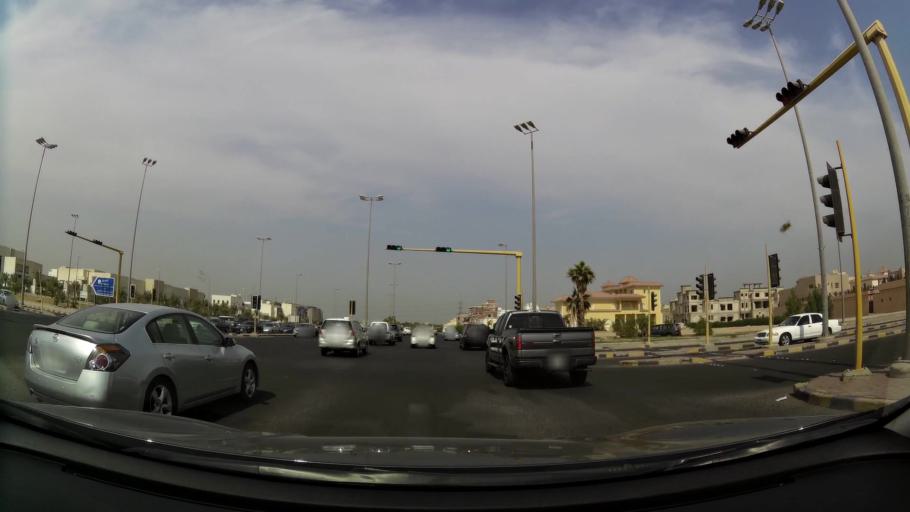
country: KW
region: Al Farwaniyah
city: Janub as Surrah
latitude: 29.2976
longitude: 48.0026
